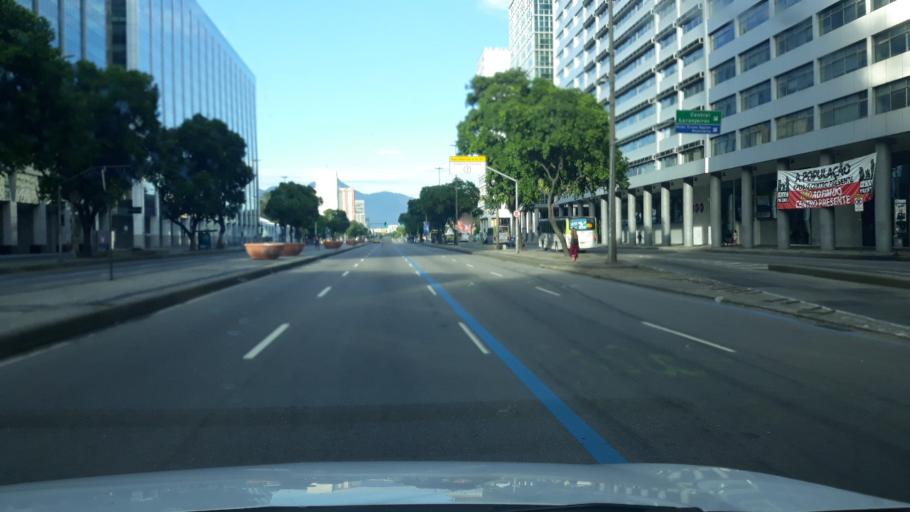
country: BR
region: Rio de Janeiro
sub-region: Rio De Janeiro
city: Rio de Janeiro
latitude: -22.9027
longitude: -43.1845
